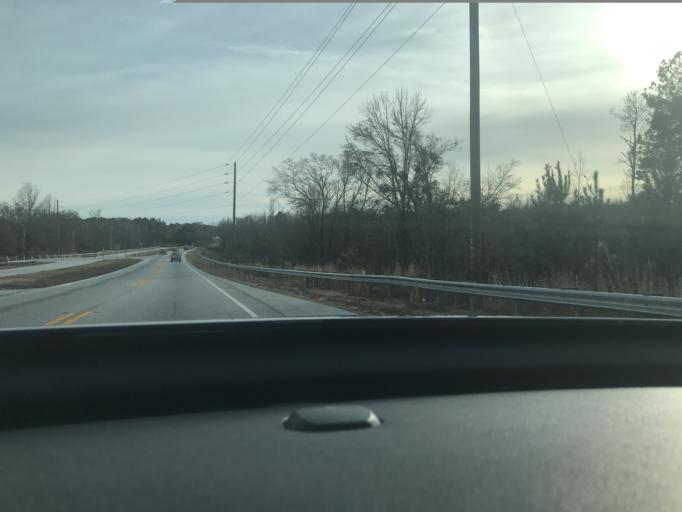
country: US
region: Georgia
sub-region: Newton County
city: Porterdale
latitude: 33.6127
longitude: -83.9200
